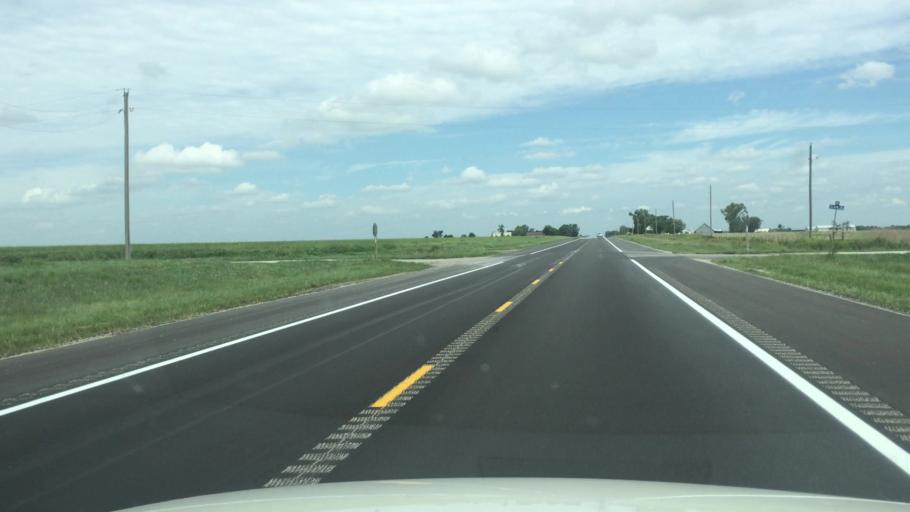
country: US
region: Kansas
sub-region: Anderson County
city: Garnett
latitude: 38.4188
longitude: -95.2487
